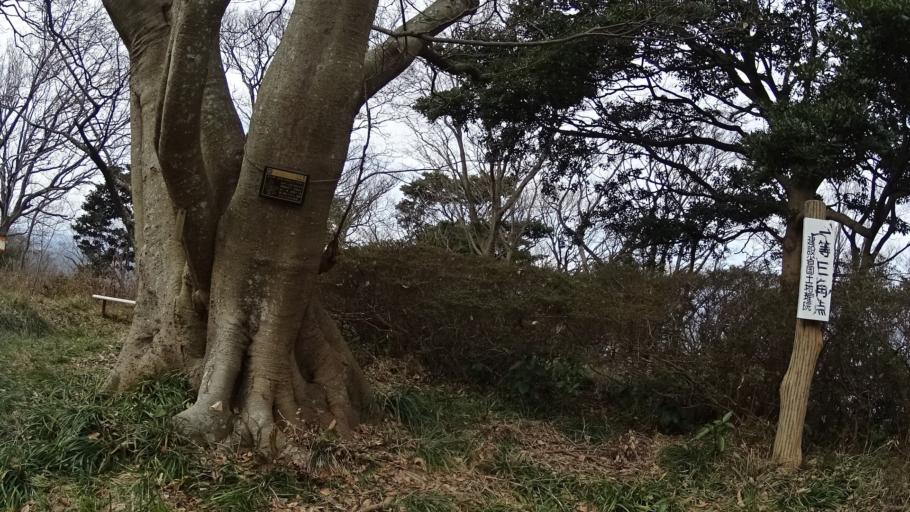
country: JP
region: Kanagawa
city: Oiso
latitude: 35.3221
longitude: 139.3123
